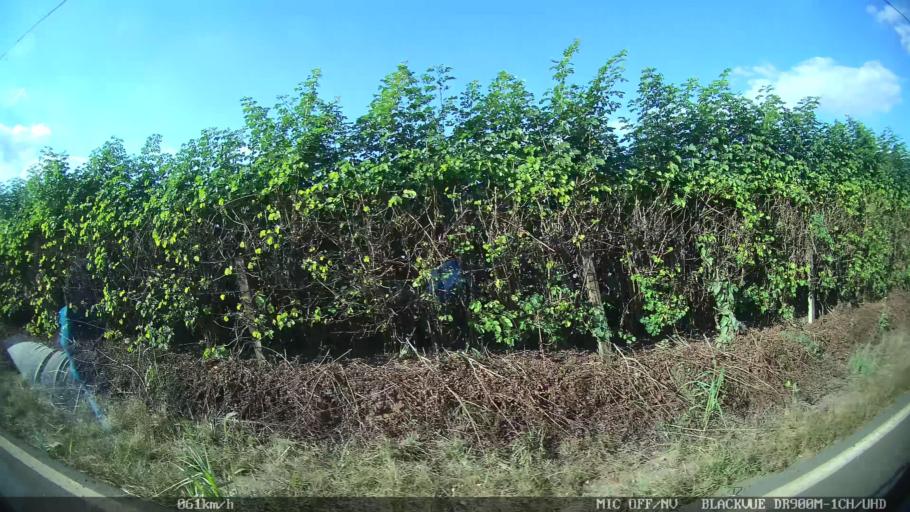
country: BR
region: Sao Paulo
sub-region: Nova Odessa
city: Nova Odessa
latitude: -22.8068
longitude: -47.3325
